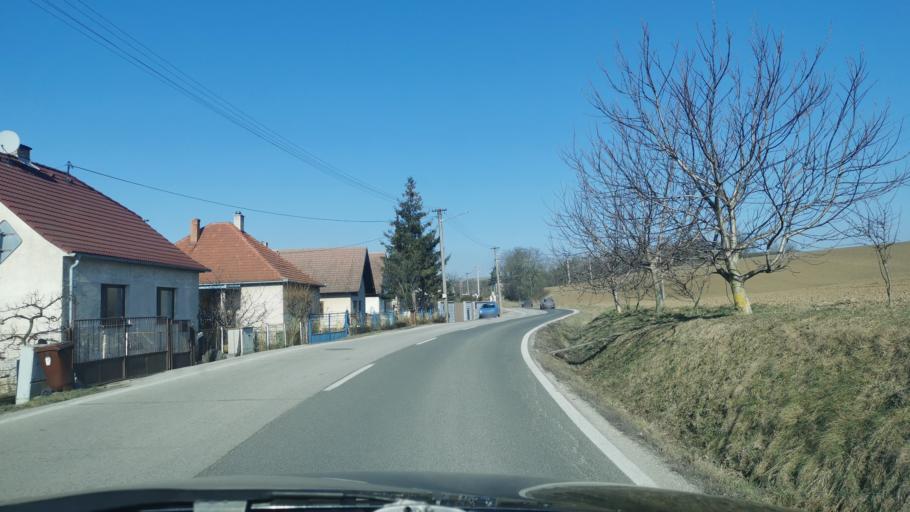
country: SK
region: Trnavsky
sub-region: Okres Senica
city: Senica
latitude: 48.6863
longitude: 17.3973
